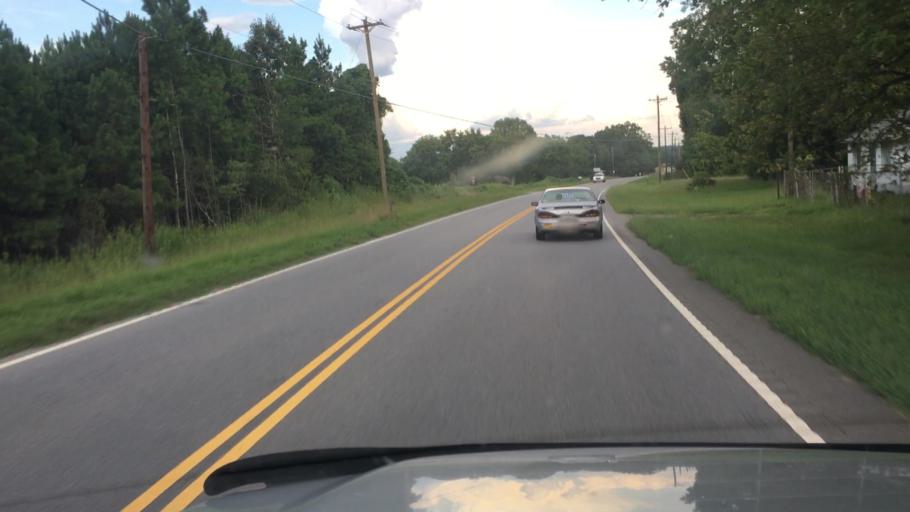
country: US
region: South Carolina
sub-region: Cherokee County
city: Gaffney
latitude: 35.1255
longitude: -81.7297
